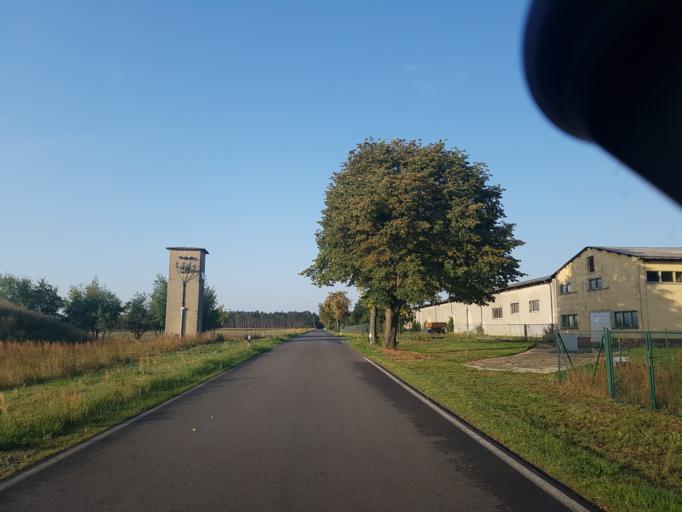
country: DE
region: Saxony-Anhalt
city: Holzdorf
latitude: 51.8120
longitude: 13.1442
